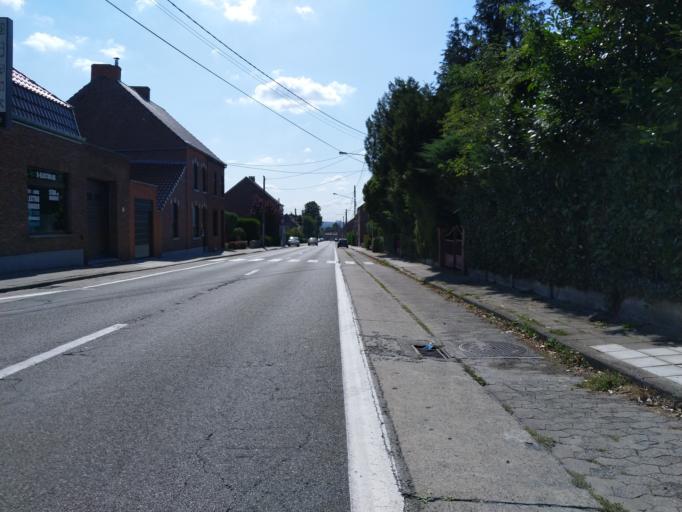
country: BE
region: Wallonia
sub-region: Province du Hainaut
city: Saint-Ghislain
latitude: 50.4880
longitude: 3.8320
